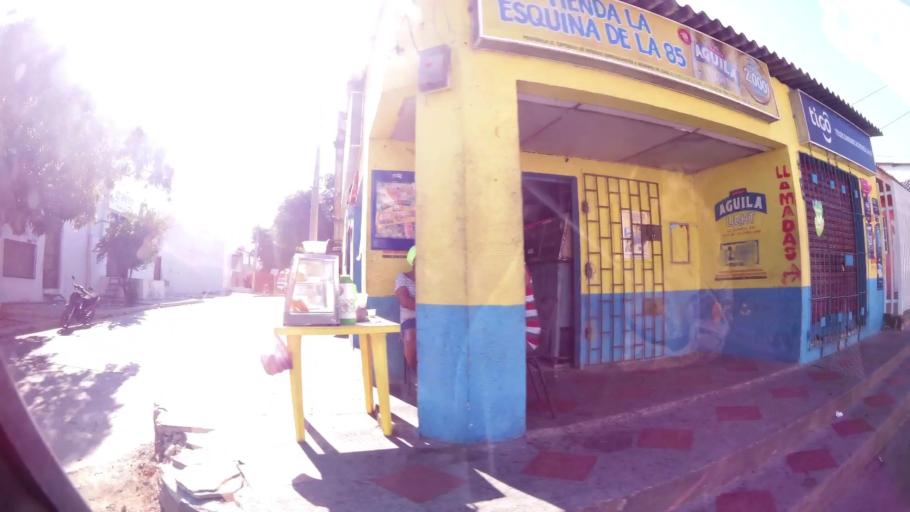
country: CO
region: Atlantico
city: Barranquilla
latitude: 11.0259
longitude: -74.8044
